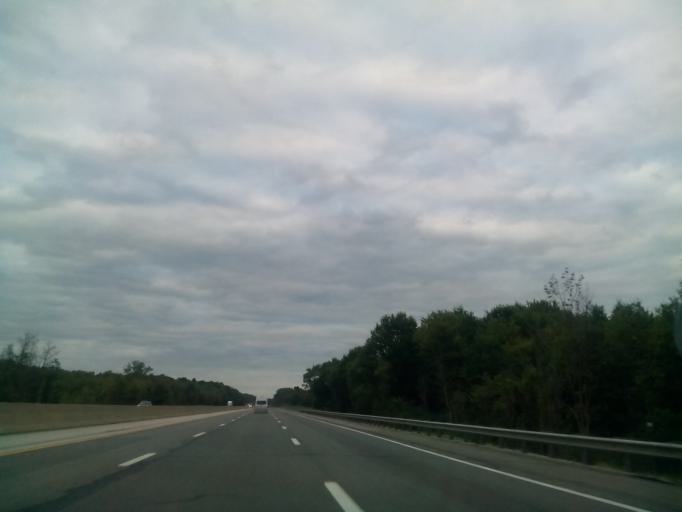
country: US
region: Ohio
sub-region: Portage County
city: Windham
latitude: 41.2414
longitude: -81.0155
